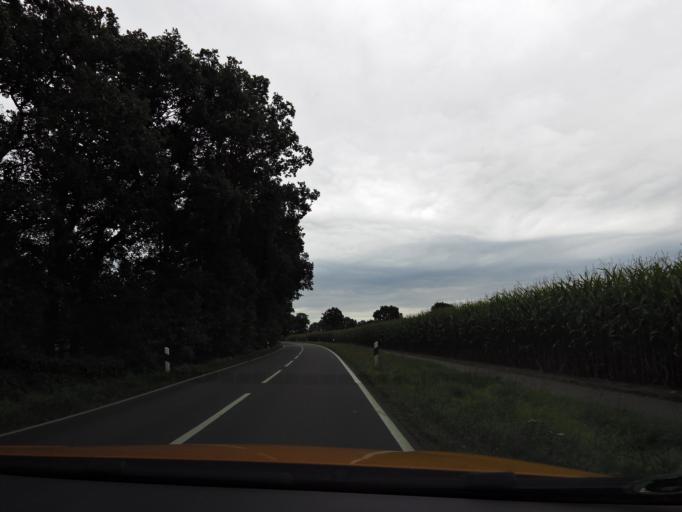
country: DE
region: Lower Saxony
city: Wiefelstede
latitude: 53.1918
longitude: 8.1439
